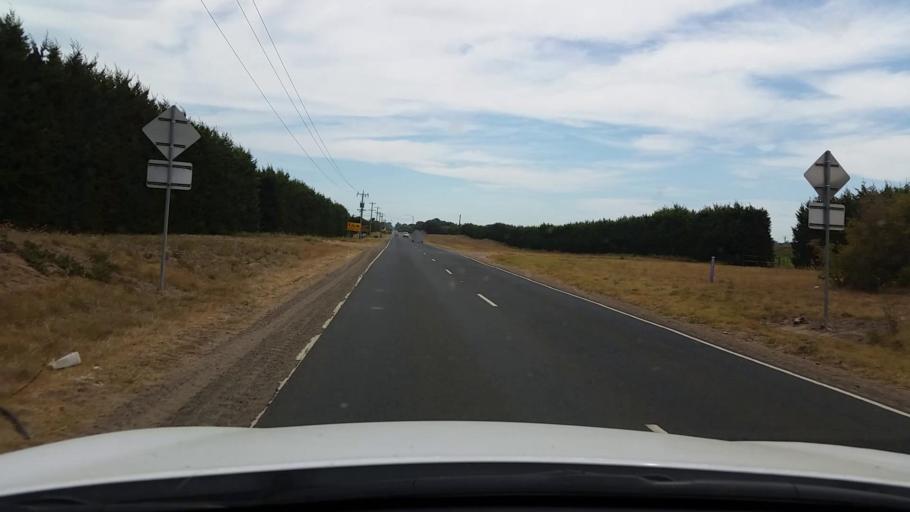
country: AU
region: Victoria
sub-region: Mornington Peninsula
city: Rosebud West
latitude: -38.4165
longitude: 144.8873
